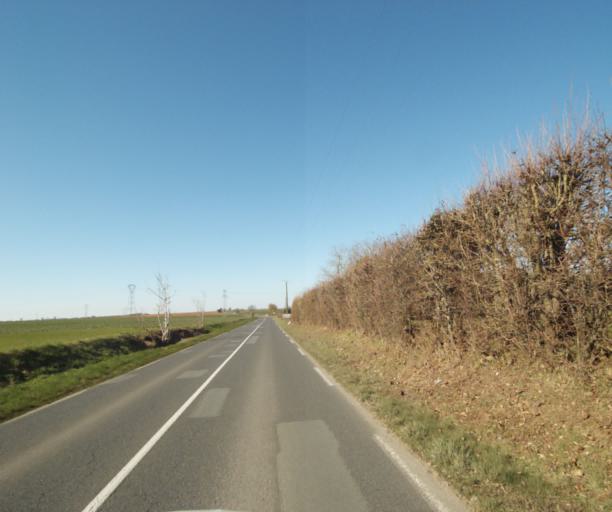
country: FR
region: Poitou-Charentes
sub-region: Departement des Deux-Sevres
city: Saint-Maxire
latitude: 46.3591
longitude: -0.4839
